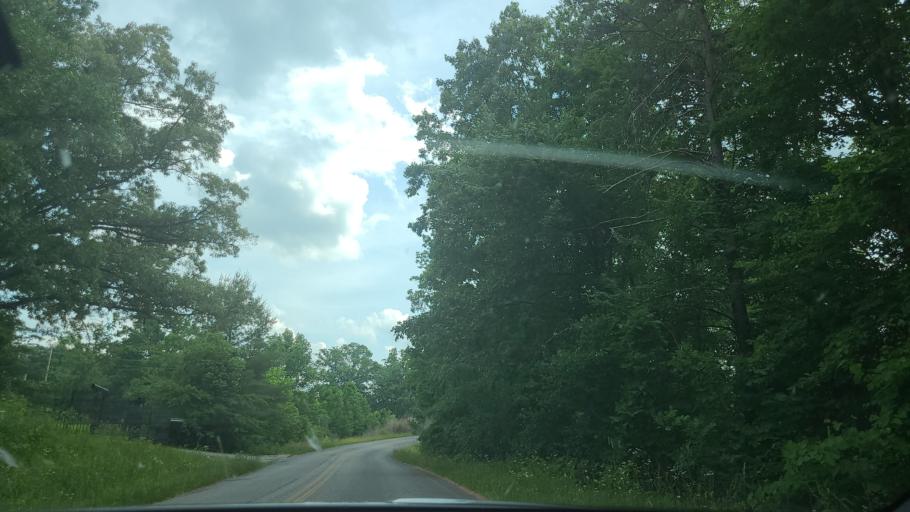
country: US
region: Tennessee
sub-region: Cumberland County
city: Lake Tansi
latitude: 35.7925
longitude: -85.0495
